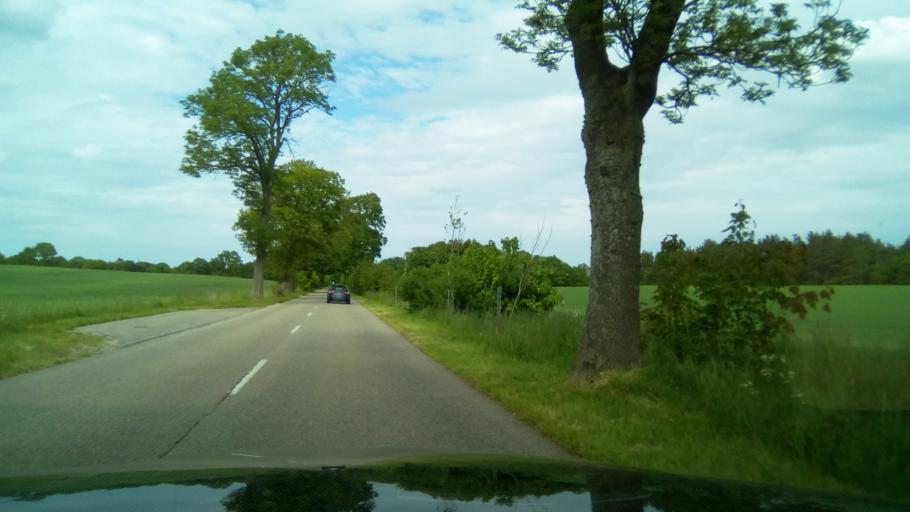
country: PL
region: Pomeranian Voivodeship
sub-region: Powiat pucki
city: Wierzchucino
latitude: 54.7746
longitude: 17.9553
